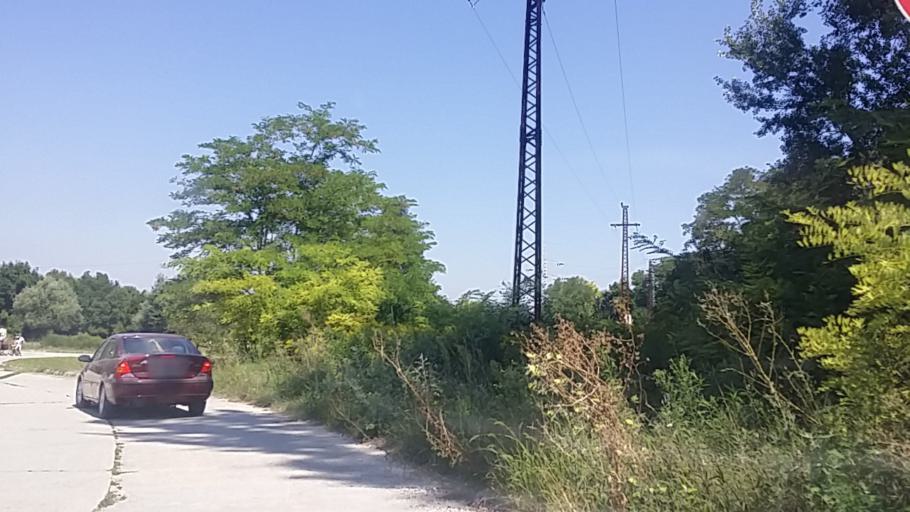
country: HU
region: Zala
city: Keszthely
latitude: 46.7041
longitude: 17.2378
